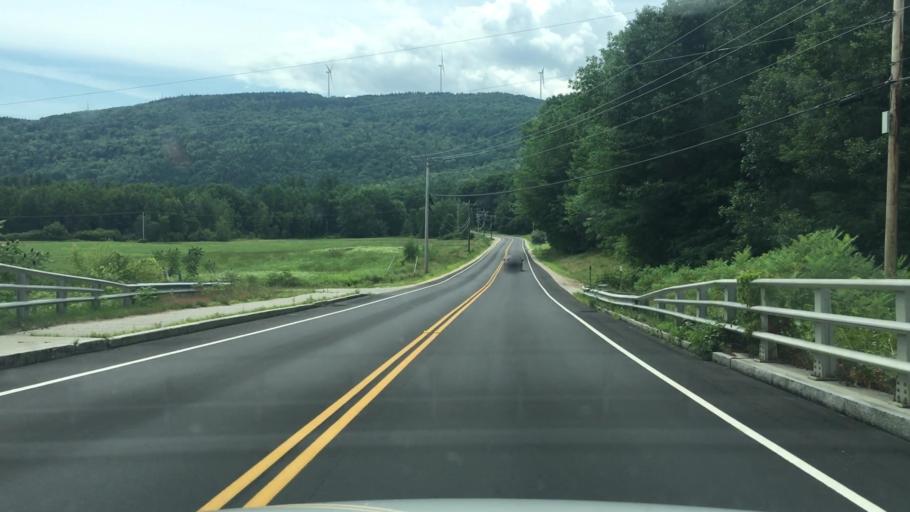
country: US
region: New Hampshire
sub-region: Grafton County
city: Rumney
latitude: 43.8009
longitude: -71.8144
